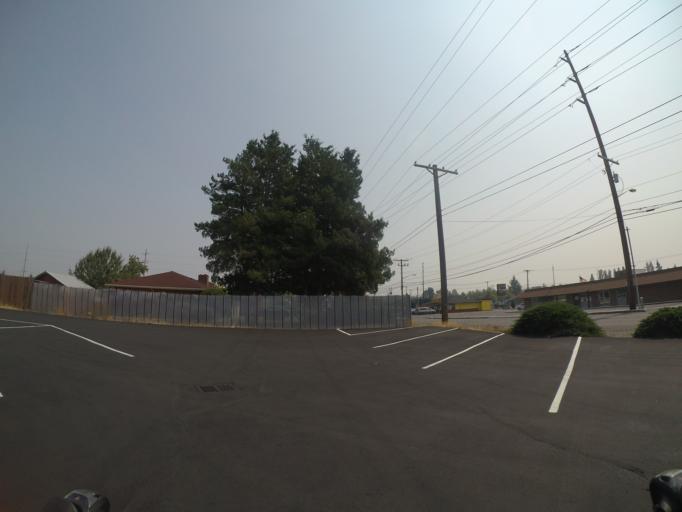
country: US
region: Washington
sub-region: Pierce County
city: Lakewood
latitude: 47.1567
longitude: -122.5064
